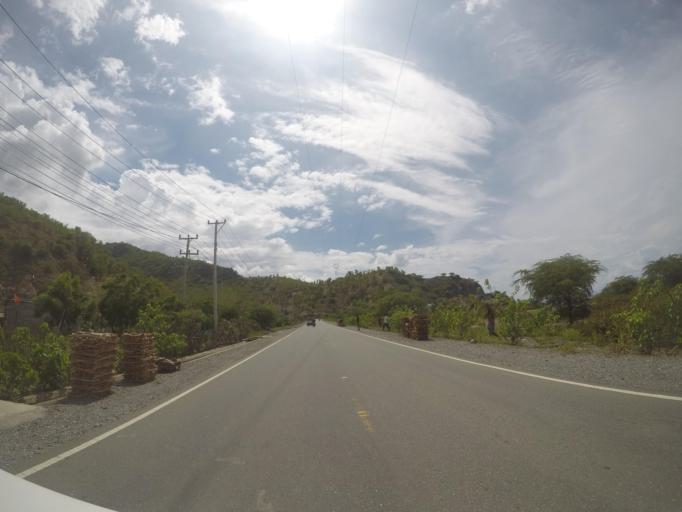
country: TL
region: Liquica
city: Liquica
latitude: -8.5735
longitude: 125.3767
